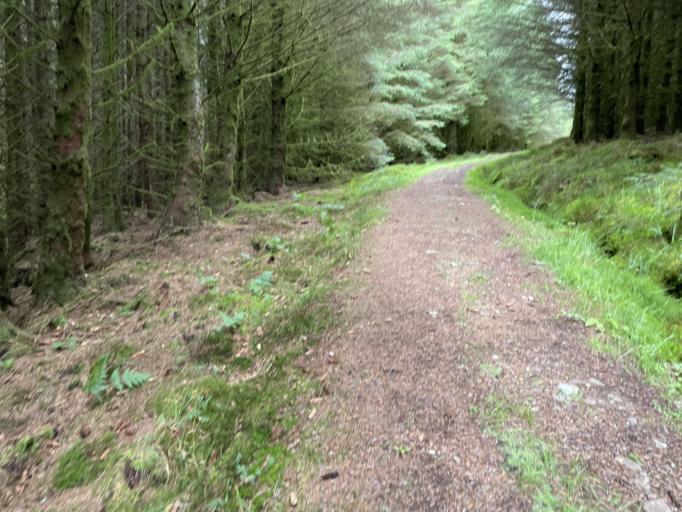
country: GB
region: Scotland
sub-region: South Ayrshire
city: Maybole
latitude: 55.1993
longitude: -4.6715
